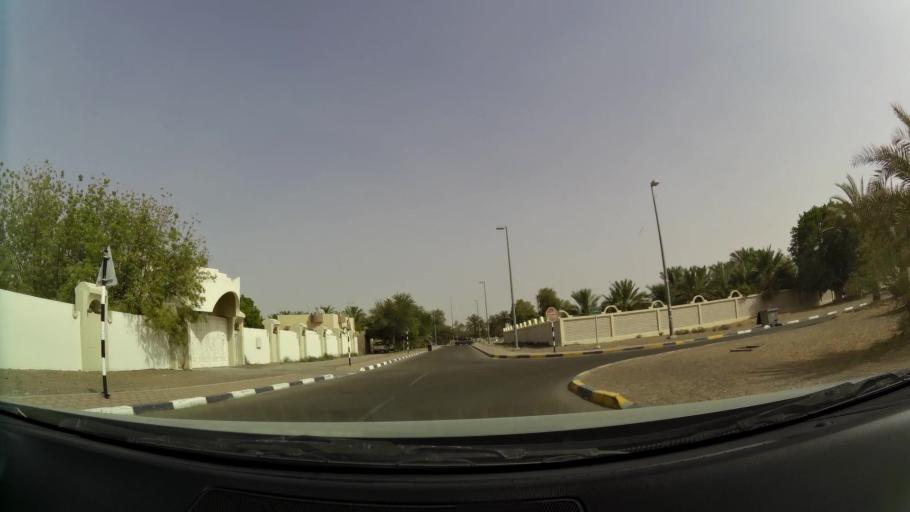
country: AE
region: Abu Dhabi
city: Al Ain
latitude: 24.1793
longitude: 55.6145
